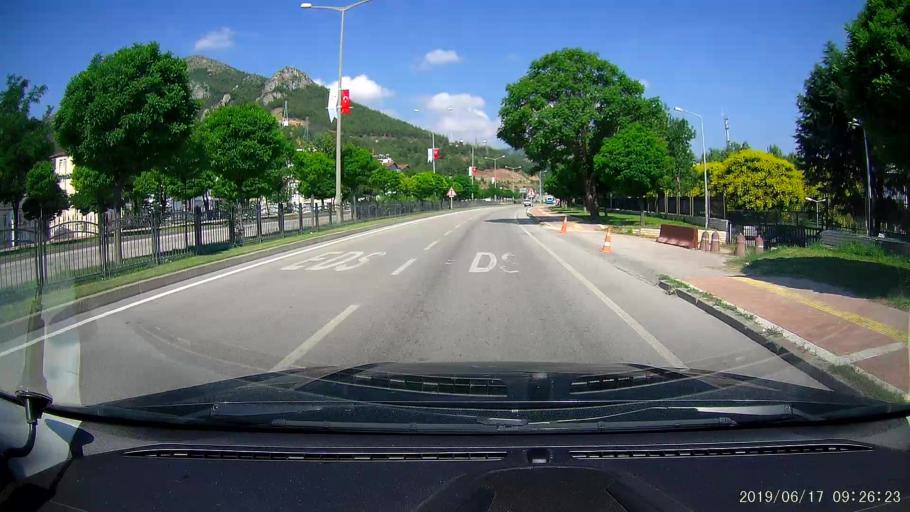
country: TR
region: Amasya
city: Amasya
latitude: 40.6692
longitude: 35.8364
